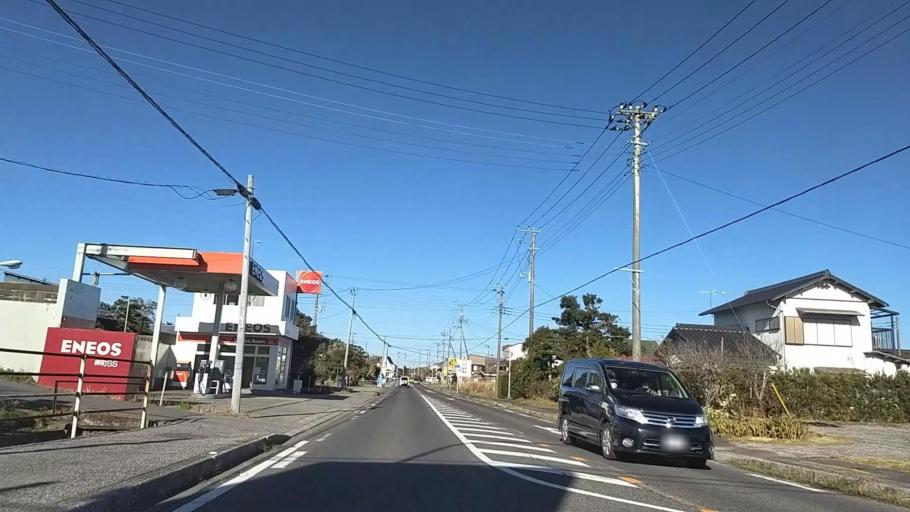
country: JP
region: Chiba
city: Ohara
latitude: 35.2941
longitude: 140.3955
